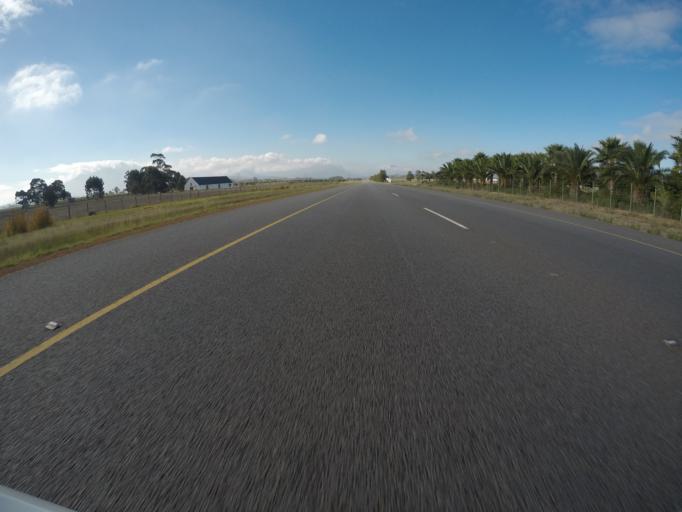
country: ZA
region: Western Cape
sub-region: City of Cape Town
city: Kraaifontein
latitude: -33.8410
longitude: 18.8003
